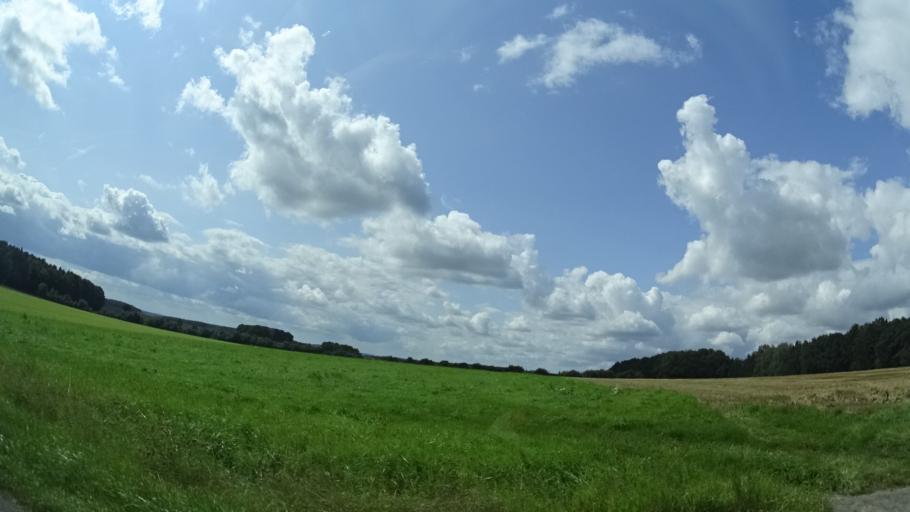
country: DE
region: Bavaria
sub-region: Upper Franconia
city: Neustadt bei Coburg
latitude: 50.2850
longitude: 11.0937
